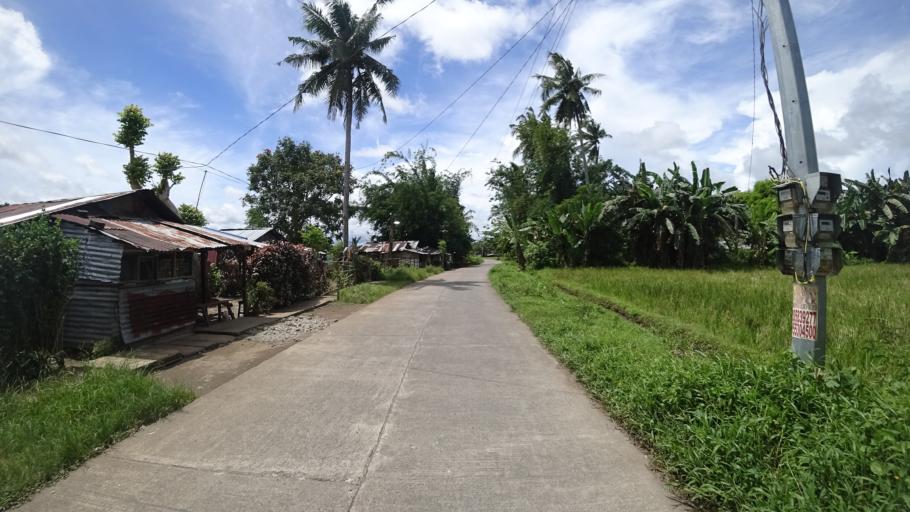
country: PH
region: Eastern Visayas
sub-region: Province of Leyte
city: Alangalang
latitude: 11.2121
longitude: 124.8456
